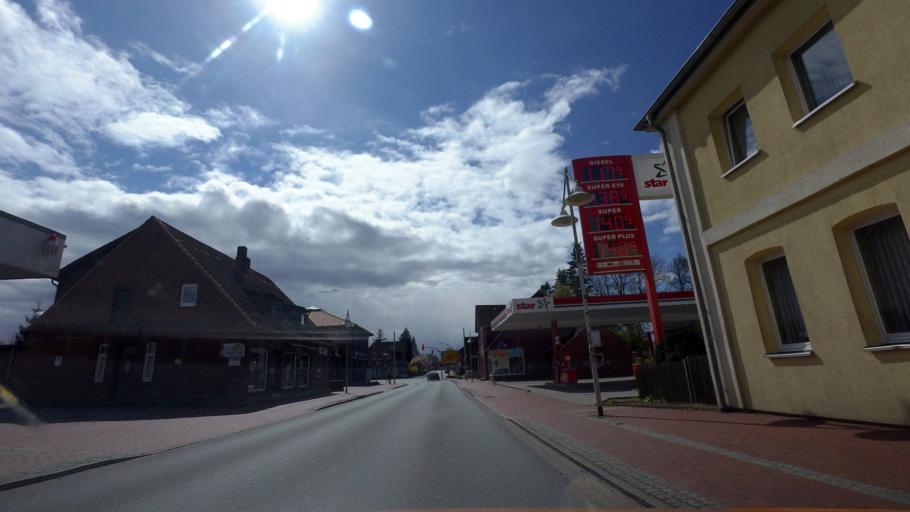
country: DE
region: Lower Saxony
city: Schneverdingen
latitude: 53.1162
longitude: 9.7888
